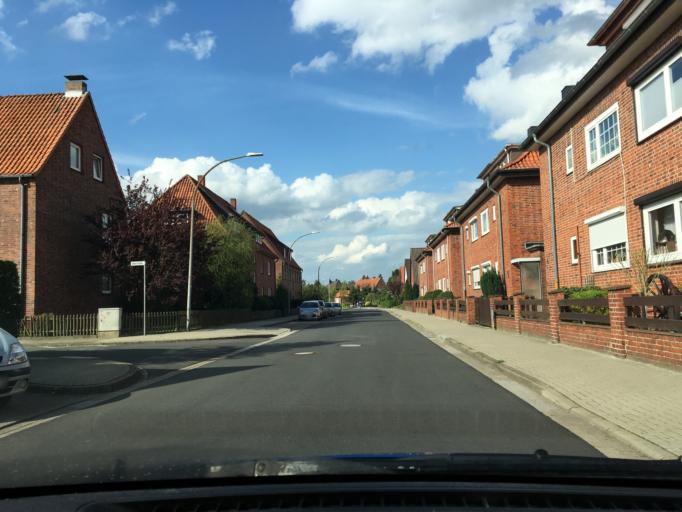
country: DE
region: Lower Saxony
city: Winsen
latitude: 53.3563
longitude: 10.2165
